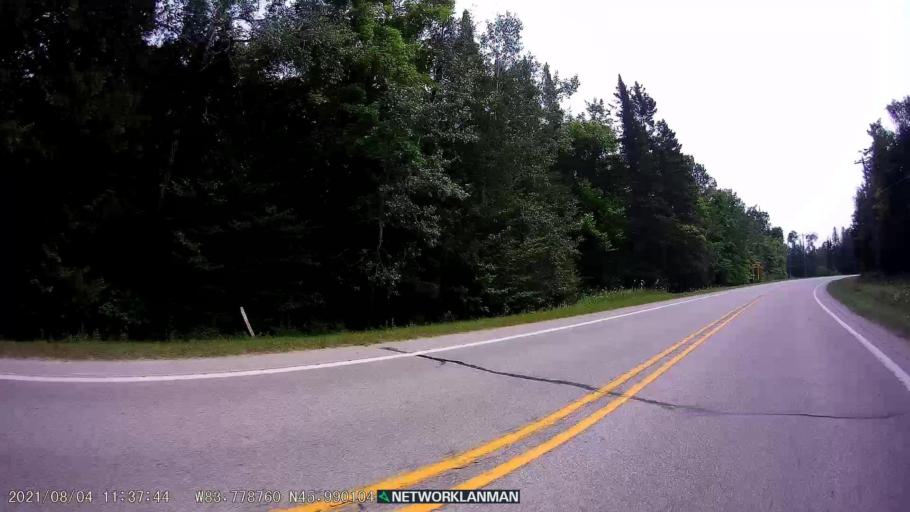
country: CA
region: Ontario
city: Thessalon
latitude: 45.9899
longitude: -83.7791
